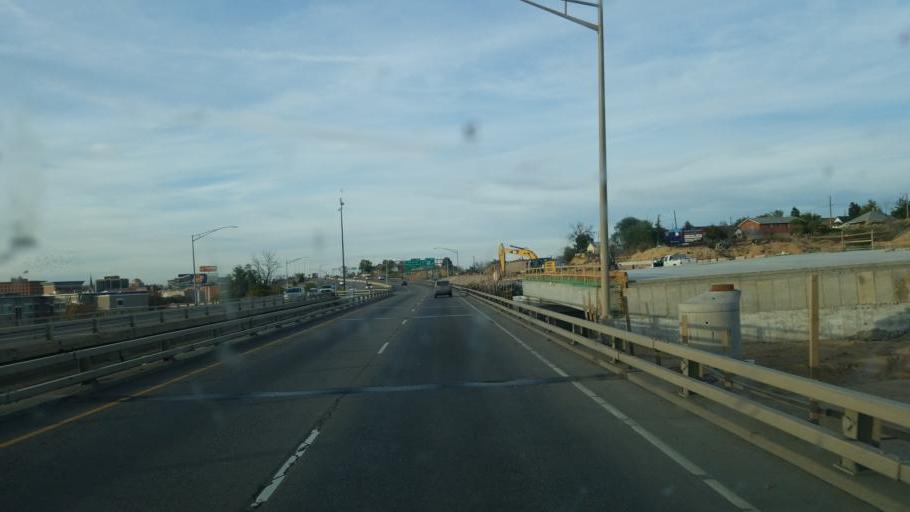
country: US
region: Colorado
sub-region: Pueblo County
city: Pueblo
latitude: 38.2645
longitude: -104.6050
